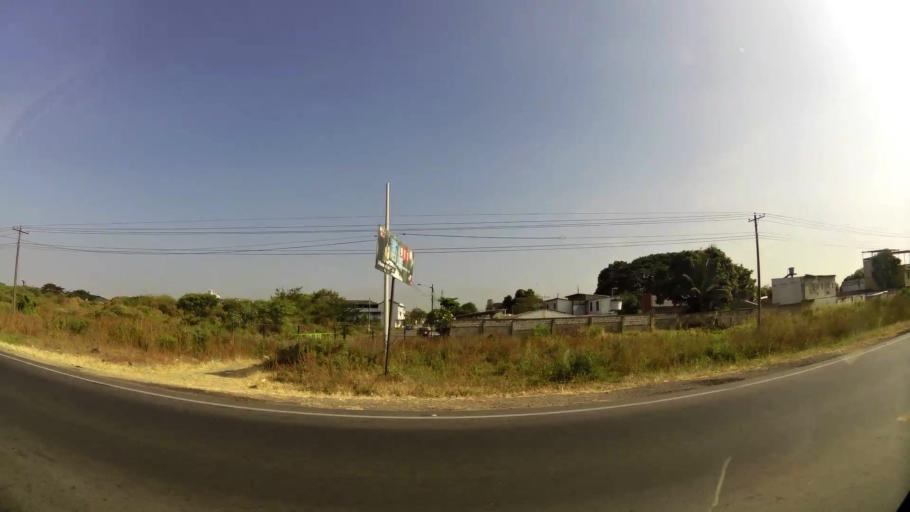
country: EC
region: Guayas
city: Eloy Alfaro
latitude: -2.1922
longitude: -79.8181
